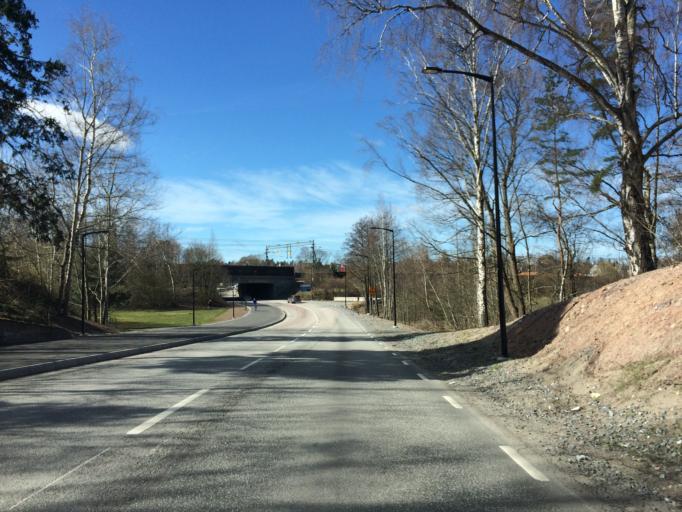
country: SE
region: Stockholm
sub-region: Sollentuna Kommun
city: Sollentuna
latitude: 59.4505
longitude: 17.9291
